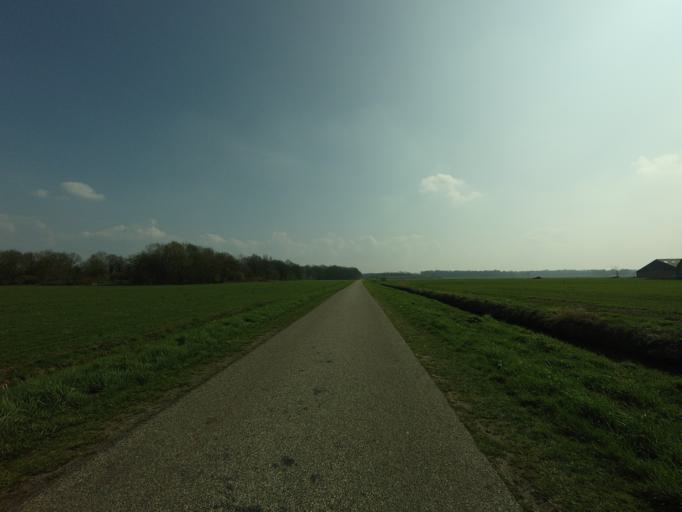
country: NL
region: North Holland
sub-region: Gemeente Bussum
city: Bussum
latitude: 52.2705
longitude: 5.1282
